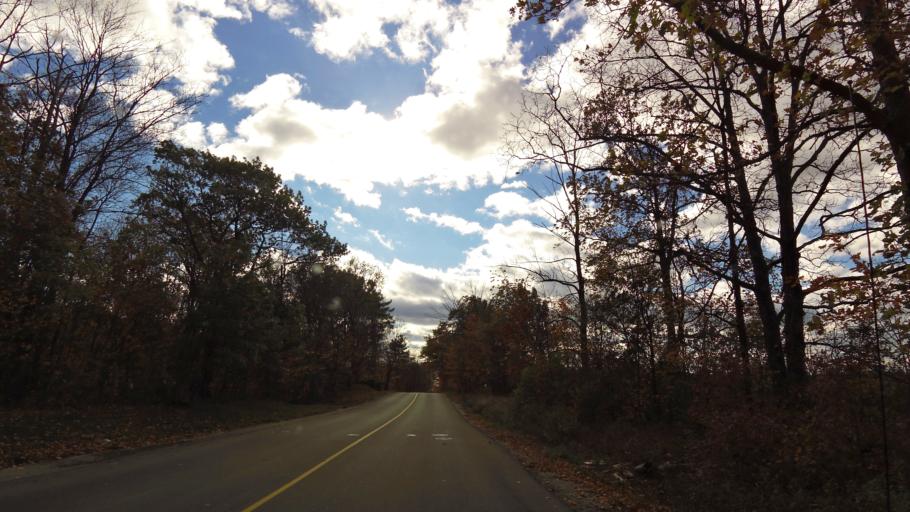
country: CA
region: Ontario
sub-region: Halton
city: Milton
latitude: 43.4730
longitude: -79.8014
